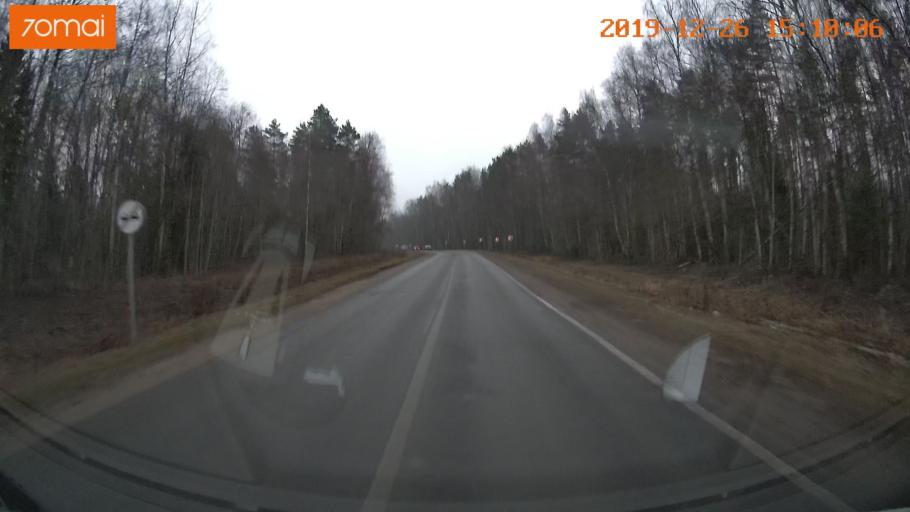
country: RU
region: Jaroslavl
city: Rybinsk
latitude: 58.1431
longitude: 38.8475
